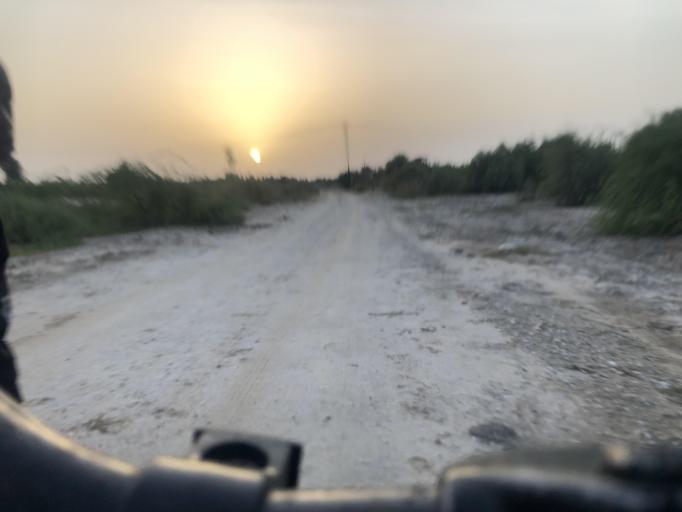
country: SN
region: Saint-Louis
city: Saint-Louis
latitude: 16.0718
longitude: -16.4323
